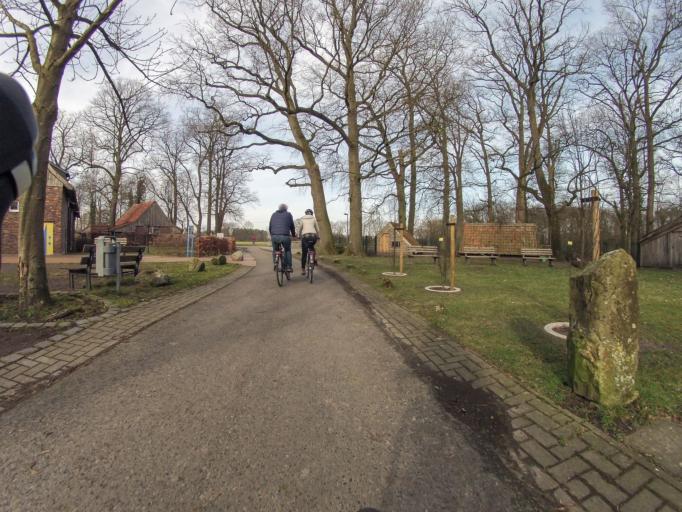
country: DE
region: North Rhine-Westphalia
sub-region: Regierungsbezirk Munster
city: Rheine
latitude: 52.3073
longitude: 7.4328
